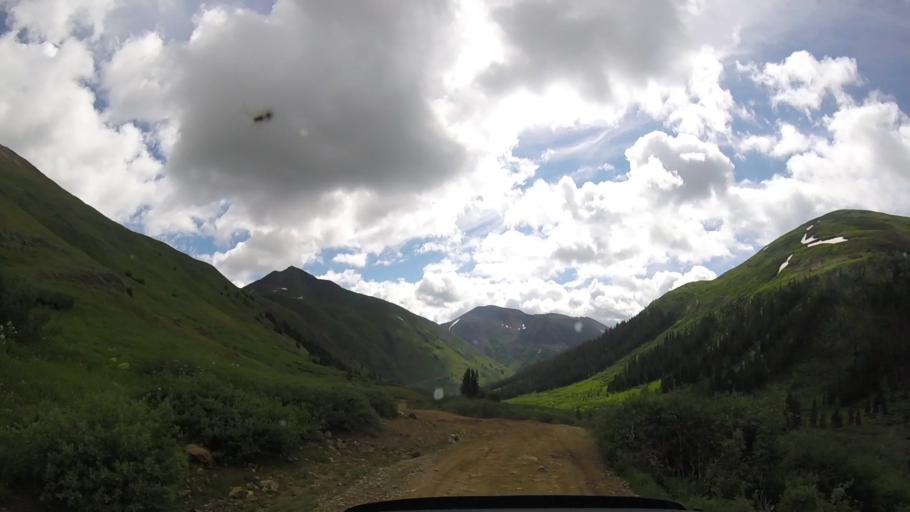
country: US
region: Colorado
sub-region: Ouray County
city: Ouray
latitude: 37.9317
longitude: -107.5888
